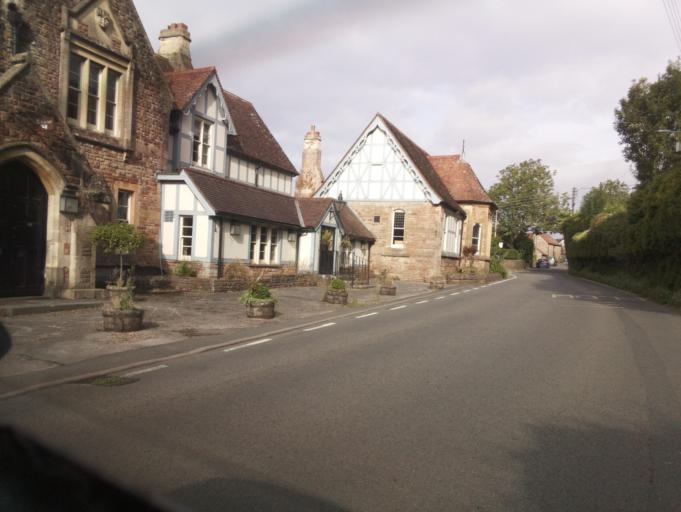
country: GB
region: England
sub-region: North Somerset
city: Nailsea
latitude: 51.4405
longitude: -2.7271
